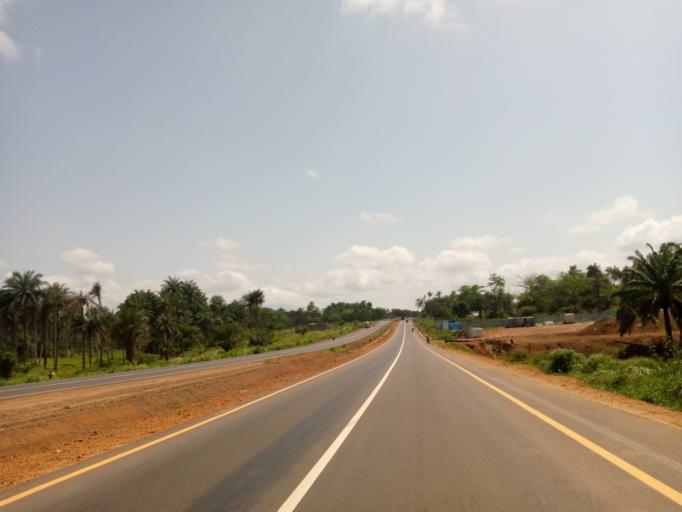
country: SL
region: Western Area
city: Waterloo
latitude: 8.3725
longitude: -12.9590
